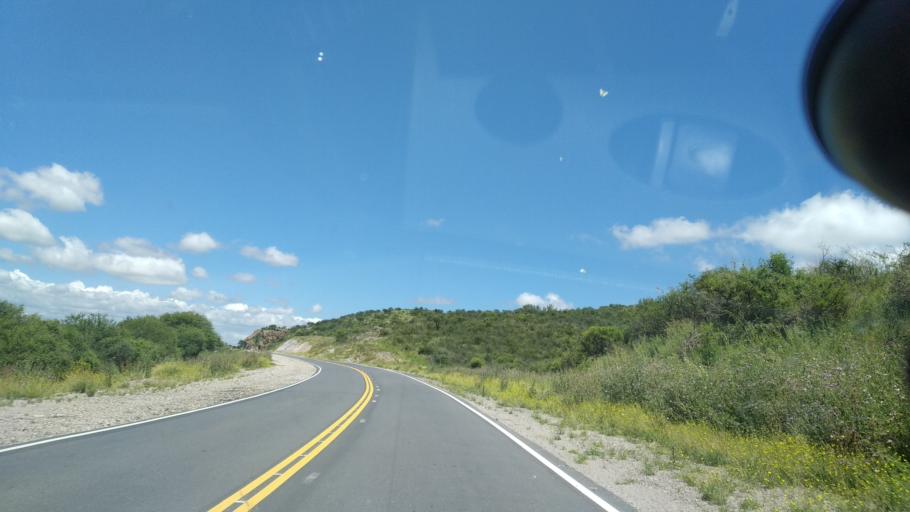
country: AR
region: Cordoba
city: Salsacate
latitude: -31.3457
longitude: -65.0983
